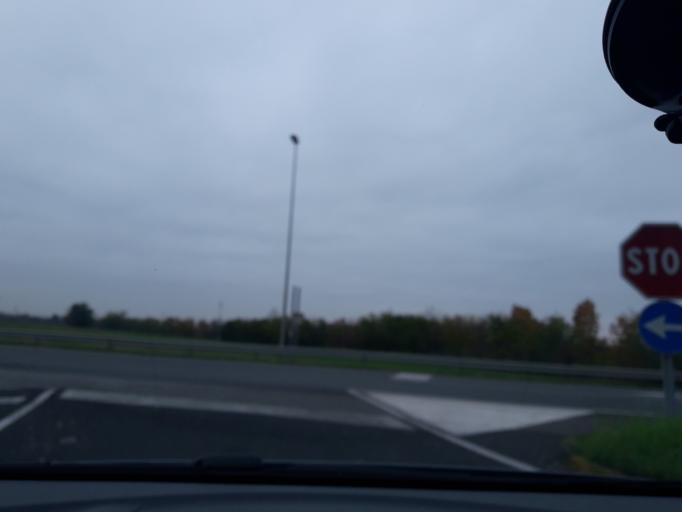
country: IT
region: Friuli Venezia Giulia
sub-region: Provincia di Udine
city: Martignacco
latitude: 46.0951
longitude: 13.1214
